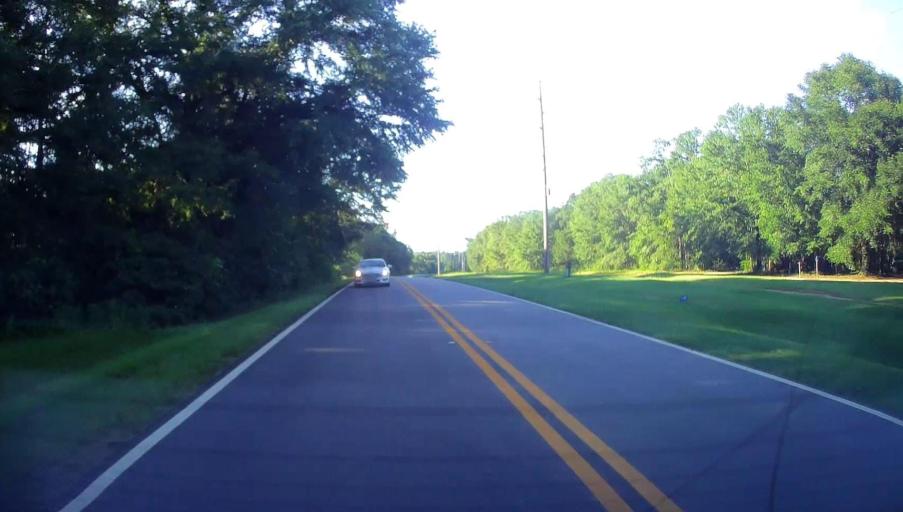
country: US
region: Georgia
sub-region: Pulaski County
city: Hawkinsville
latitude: 32.2940
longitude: -83.4496
